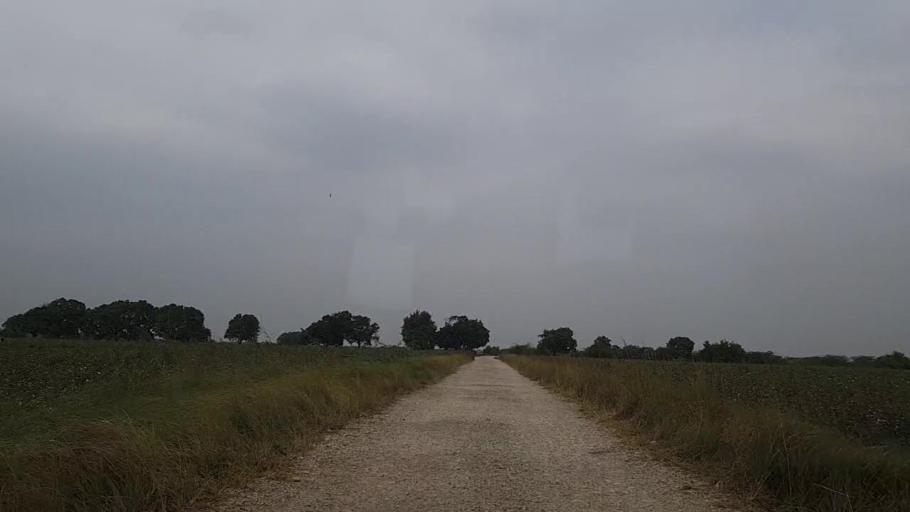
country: PK
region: Sindh
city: Mirpur Sakro
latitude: 24.6195
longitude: 67.7175
